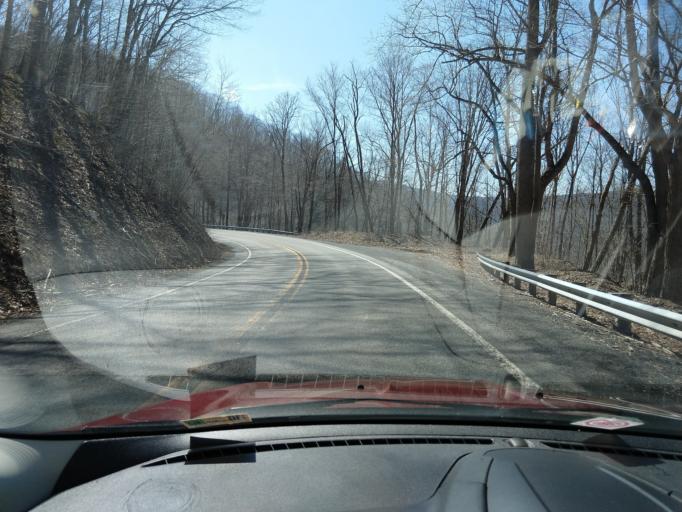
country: US
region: West Virginia
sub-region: Summers County
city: Hinton
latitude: 37.7516
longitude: -80.9053
